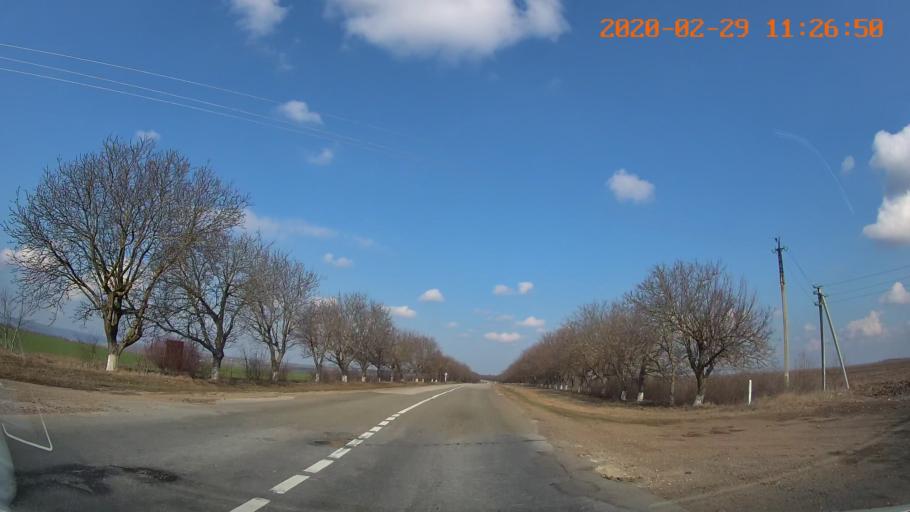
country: MD
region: Telenesti
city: Cocieri
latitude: 47.4590
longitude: 29.1444
